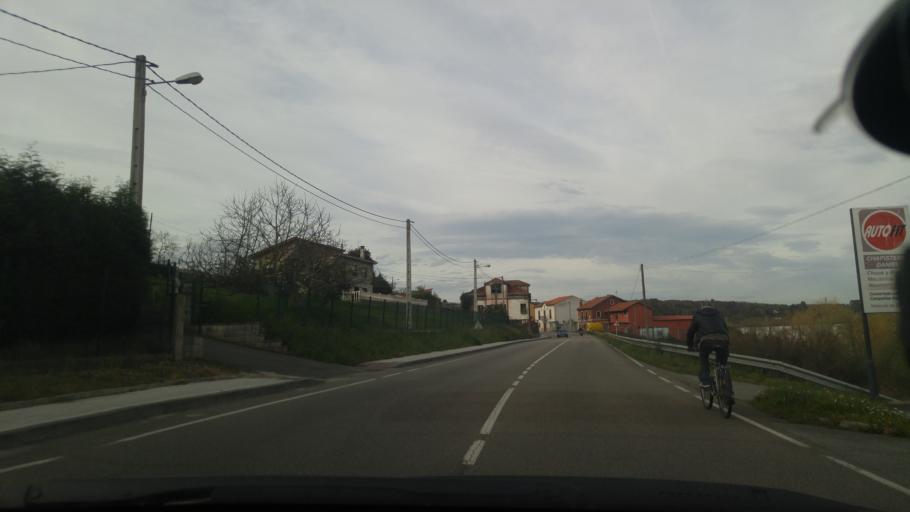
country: ES
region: Asturias
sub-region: Province of Asturias
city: Corvera de Asturias
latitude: 43.5204
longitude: -5.8709
